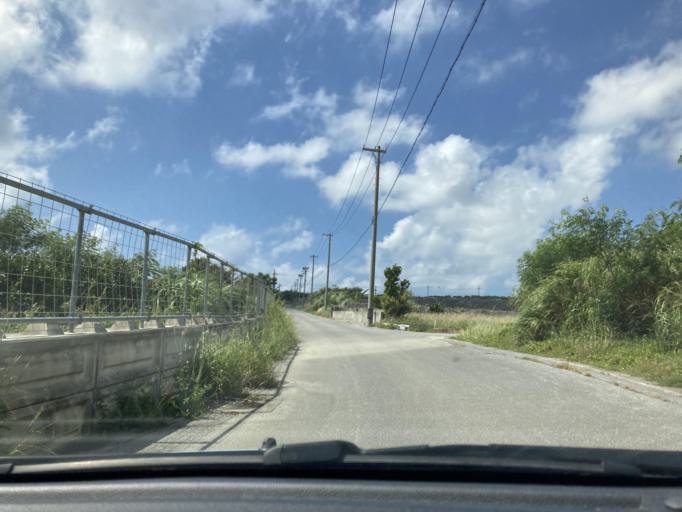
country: JP
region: Okinawa
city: Itoman
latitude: 26.1015
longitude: 127.7326
